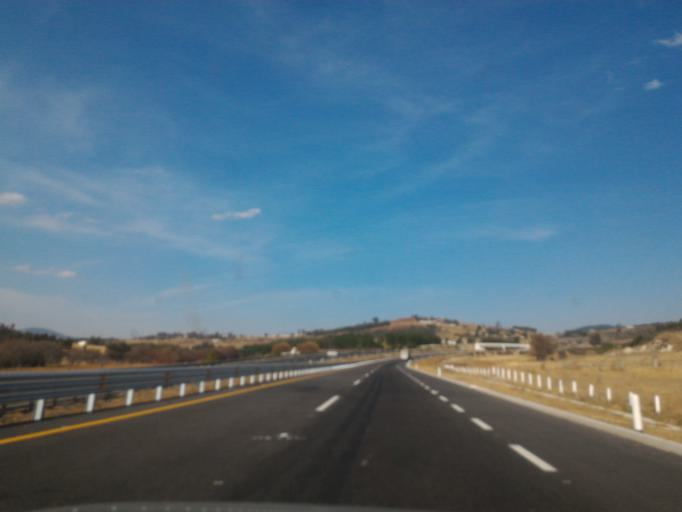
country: MX
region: Mexico
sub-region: Atlacomulco
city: San Bartolo Lanzados
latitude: 19.8640
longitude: -99.8756
